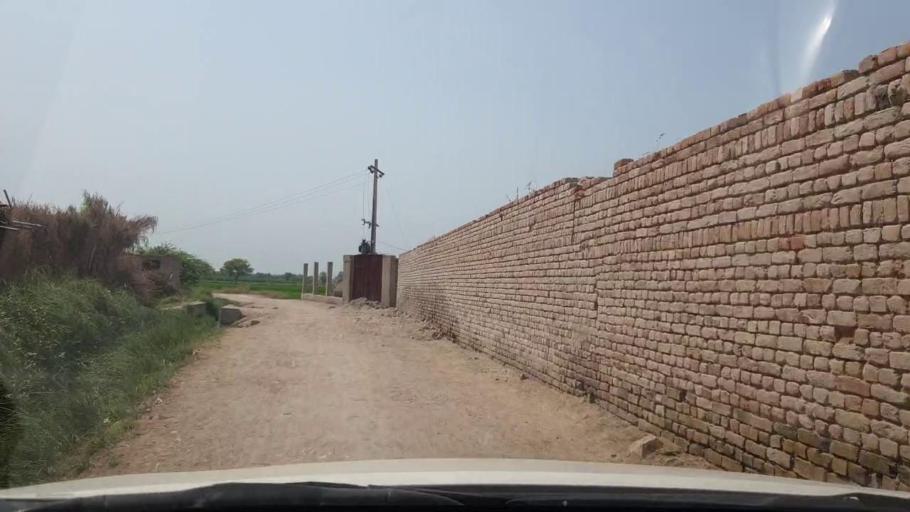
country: PK
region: Sindh
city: Shikarpur
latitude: 27.9908
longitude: 68.7124
